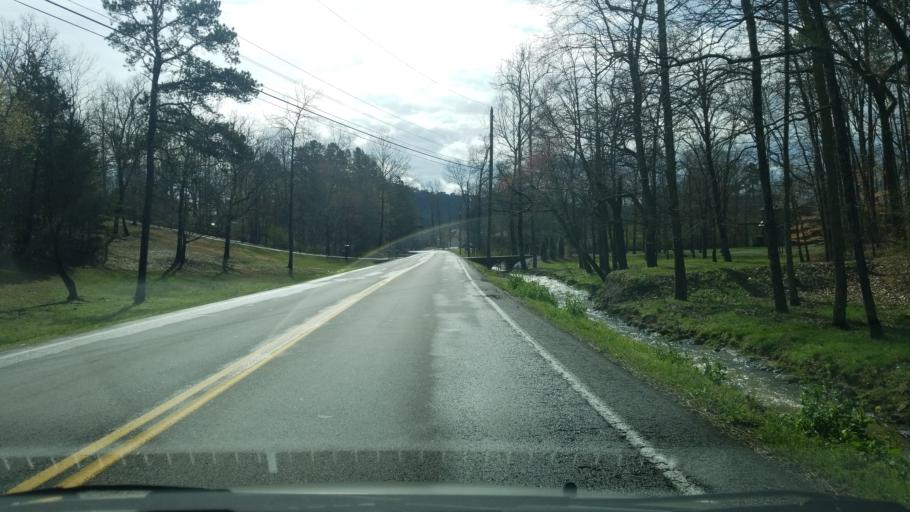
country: US
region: Tennessee
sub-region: Hamilton County
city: Collegedale
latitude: 35.0173
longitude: -85.0945
